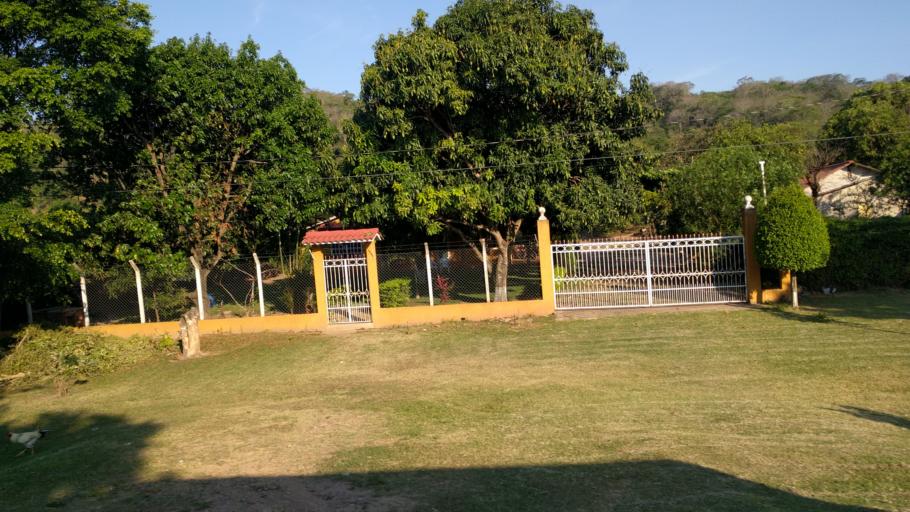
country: BO
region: Santa Cruz
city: Jorochito
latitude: -18.0797
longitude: -63.4477
